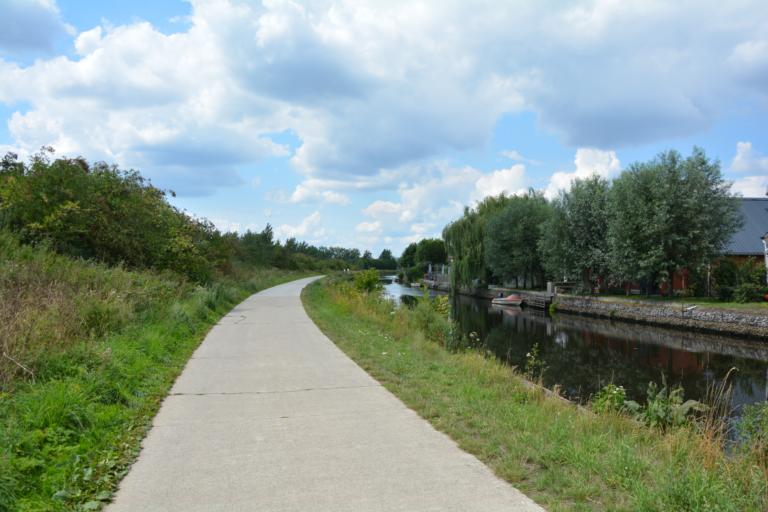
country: BE
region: Flanders
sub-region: Provincie Oost-Vlaanderen
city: Moerbeke
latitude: 51.1717
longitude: 3.9451
